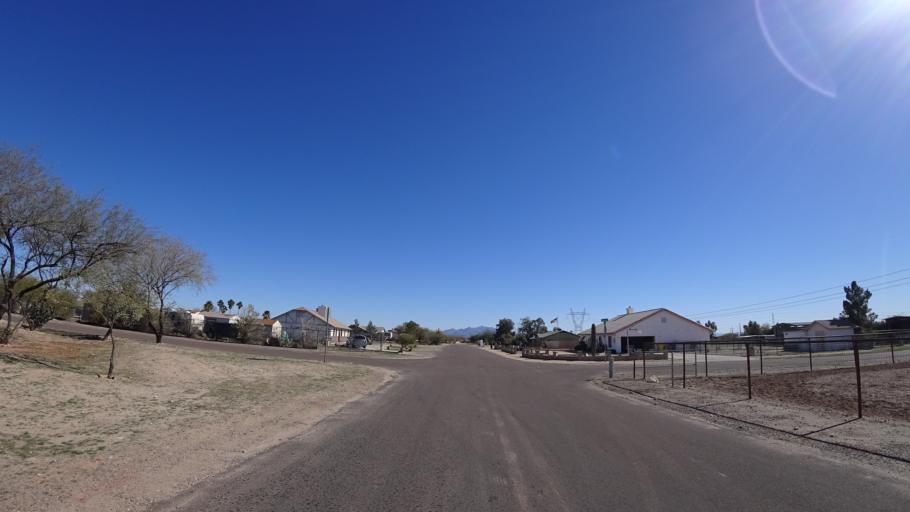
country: US
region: Arizona
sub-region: Maricopa County
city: Buckeye
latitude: 33.4255
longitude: -112.5332
